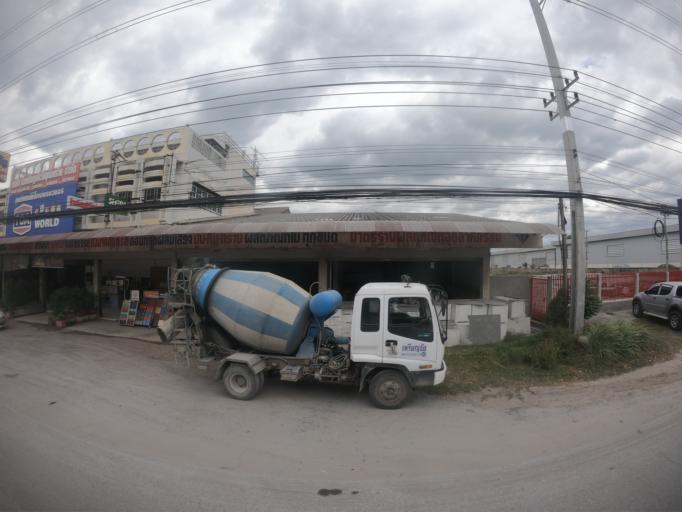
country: TH
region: Nakhon Ratchasima
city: Nakhon Ratchasima
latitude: 14.9418
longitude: 102.1305
